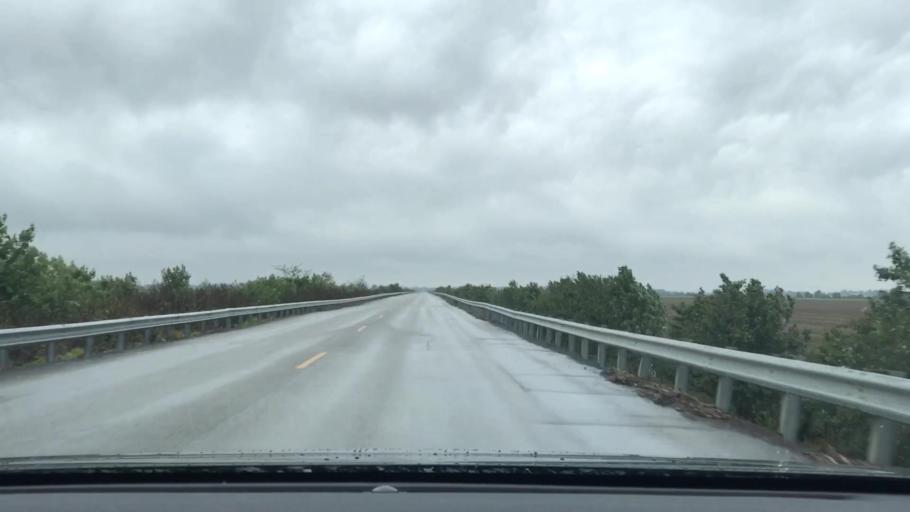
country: US
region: Kentucky
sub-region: McLean County
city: Calhoun
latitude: 37.3893
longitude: -87.3211
